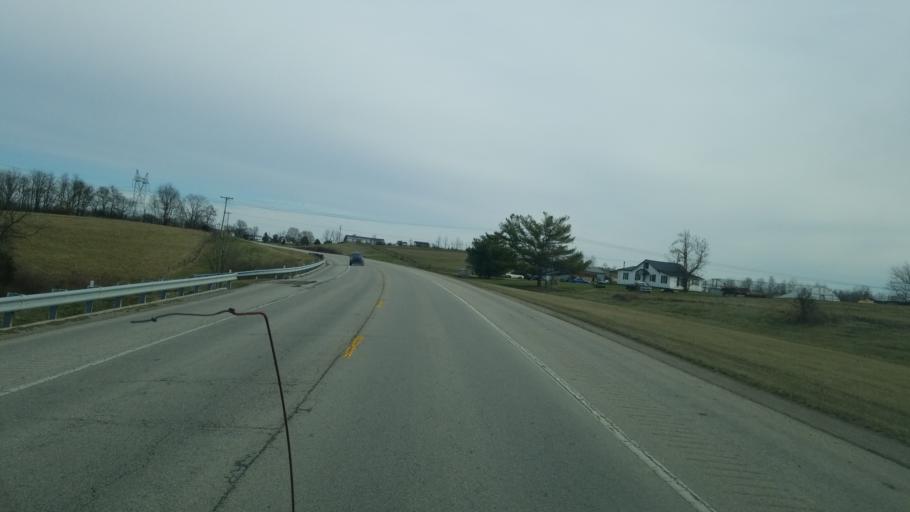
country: US
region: Kentucky
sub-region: Robertson County
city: Mount Olivet
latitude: 38.4775
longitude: -83.8883
